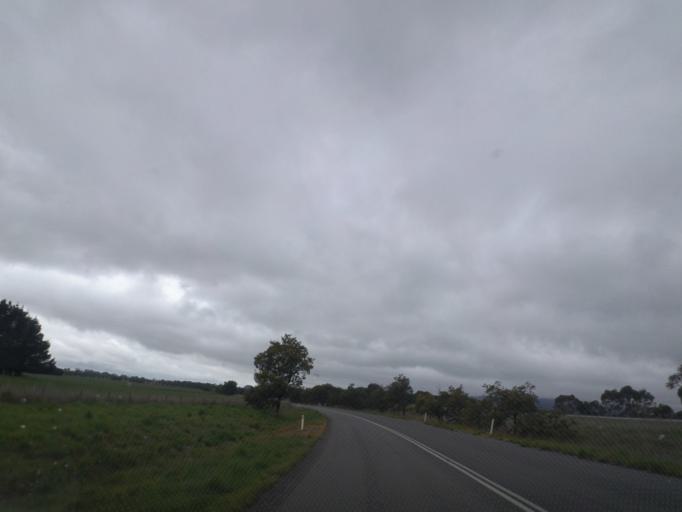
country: AU
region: Victoria
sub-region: Hume
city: Sunbury
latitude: -37.3205
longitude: 144.5302
